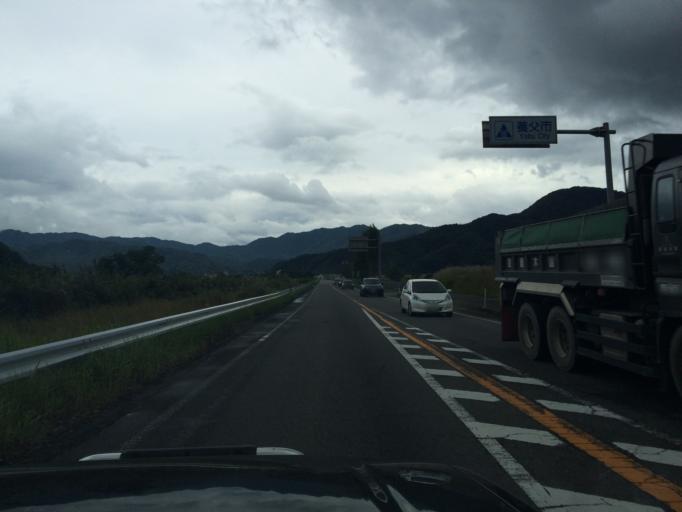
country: JP
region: Hyogo
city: Toyooka
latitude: 35.4472
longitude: 134.7718
